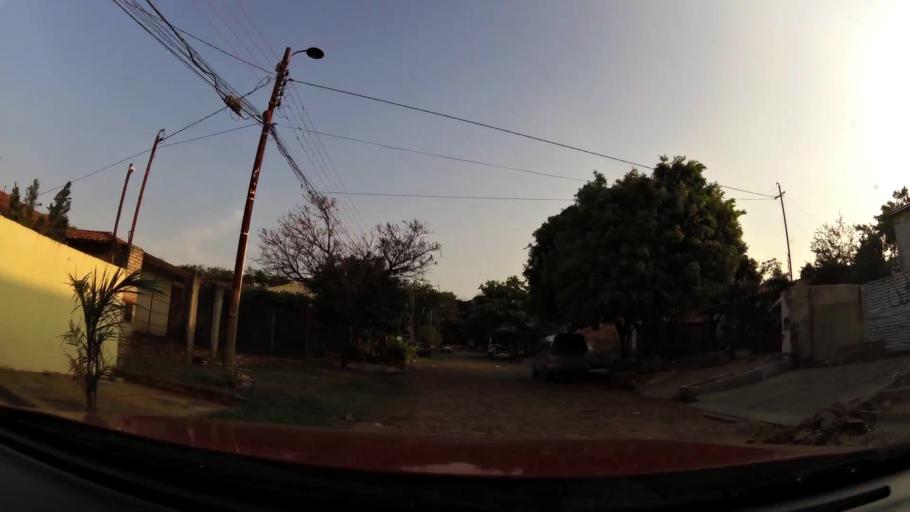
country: PY
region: Central
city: Lambare
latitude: -25.3522
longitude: -57.6013
